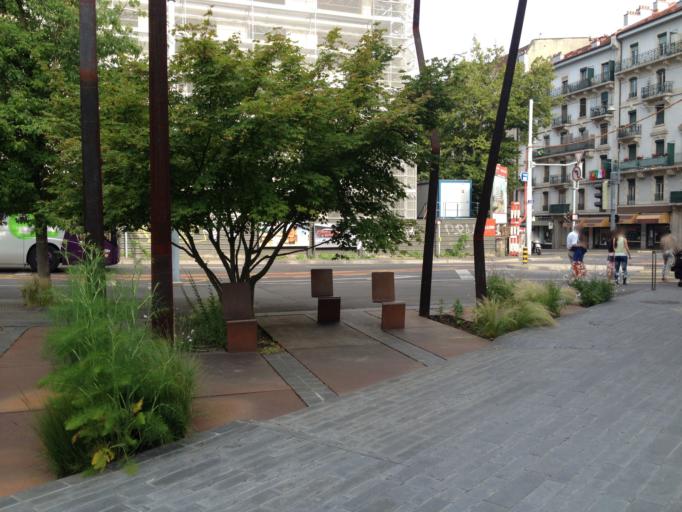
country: CH
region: Geneva
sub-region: Geneva
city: Chene-Bougeries
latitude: 46.1997
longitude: 6.1677
